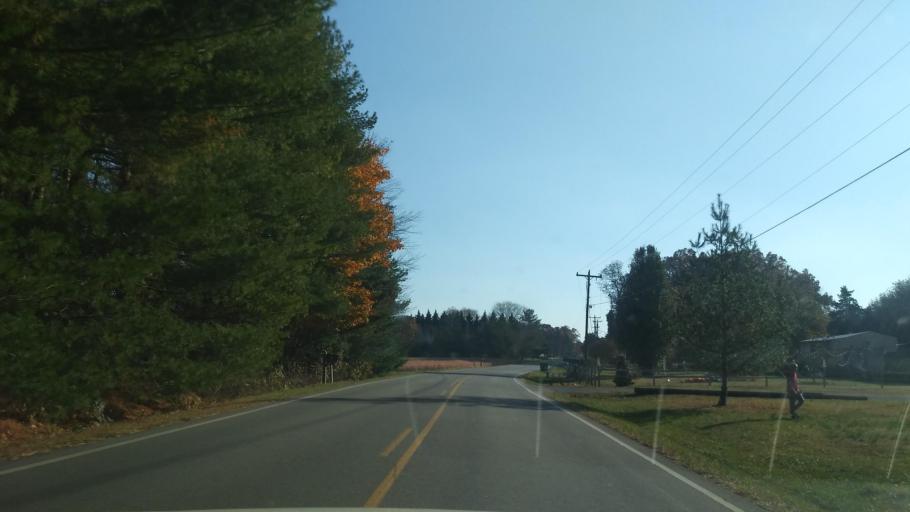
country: US
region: North Carolina
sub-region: Rockingham County
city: Reidsville
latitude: 36.2568
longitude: -79.7229
